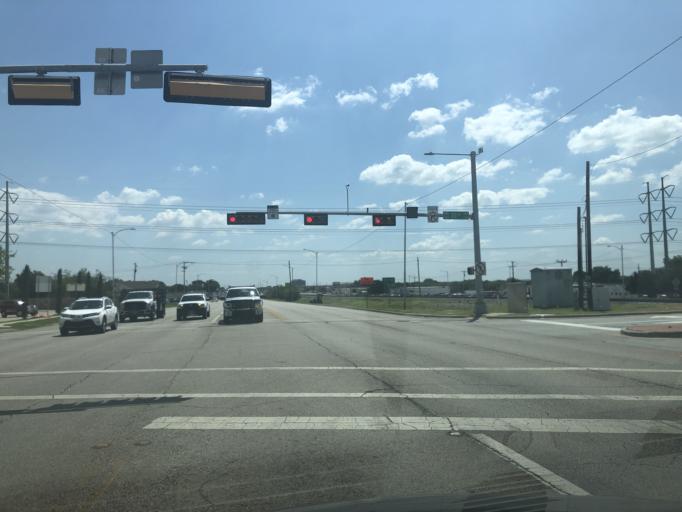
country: US
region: Texas
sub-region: Dallas County
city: Grand Prairie
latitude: 32.7395
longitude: -97.0370
